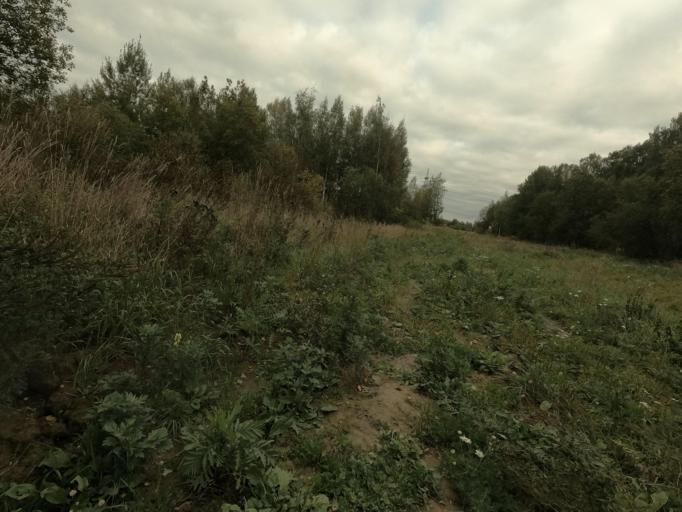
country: RU
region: St.-Petersburg
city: Metallostroy
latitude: 59.8162
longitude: 30.5439
